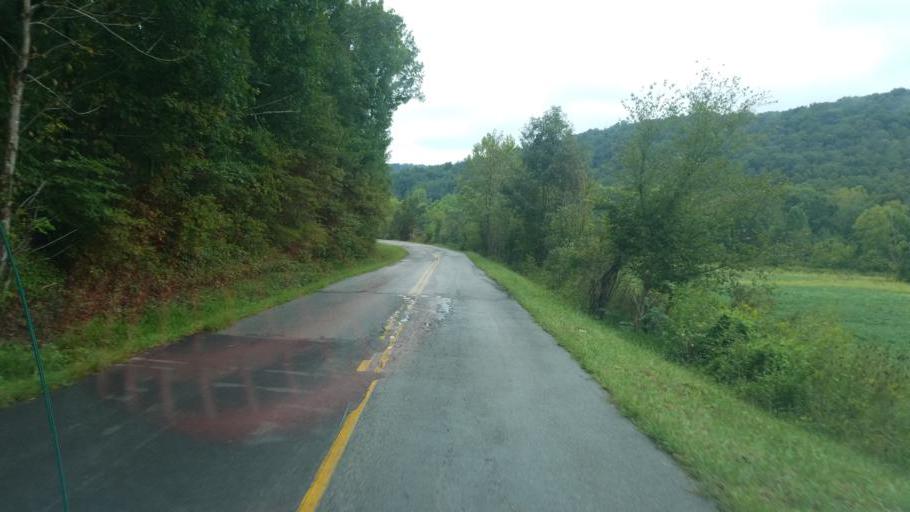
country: US
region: Kentucky
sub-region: Fleming County
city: Flemingsburg
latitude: 38.3650
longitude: -83.5344
